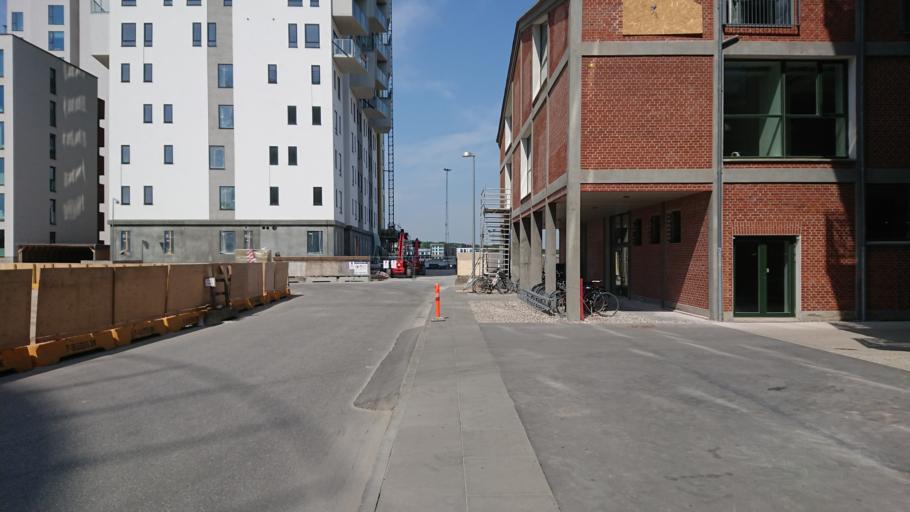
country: DK
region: North Denmark
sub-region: Alborg Kommune
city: Aalborg
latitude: 57.0476
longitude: 9.9366
